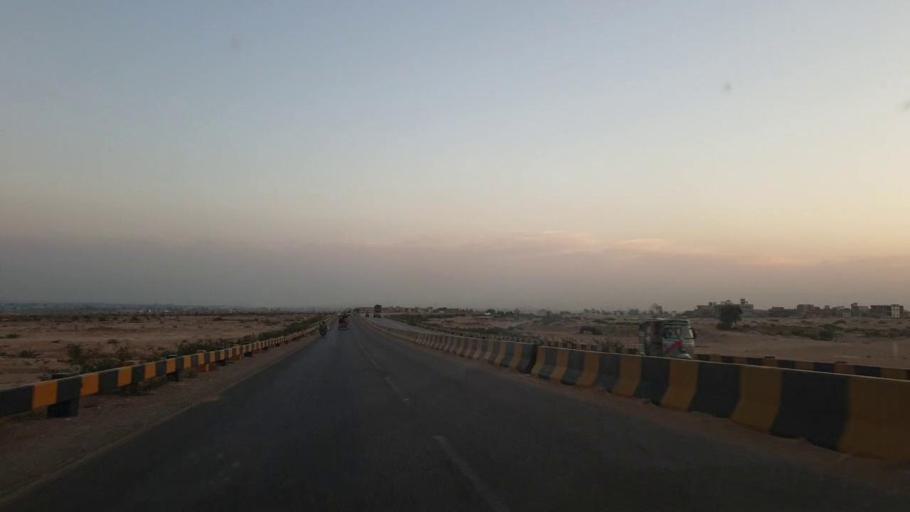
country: PK
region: Sindh
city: Jamshoro
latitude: 25.3971
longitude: 68.2736
